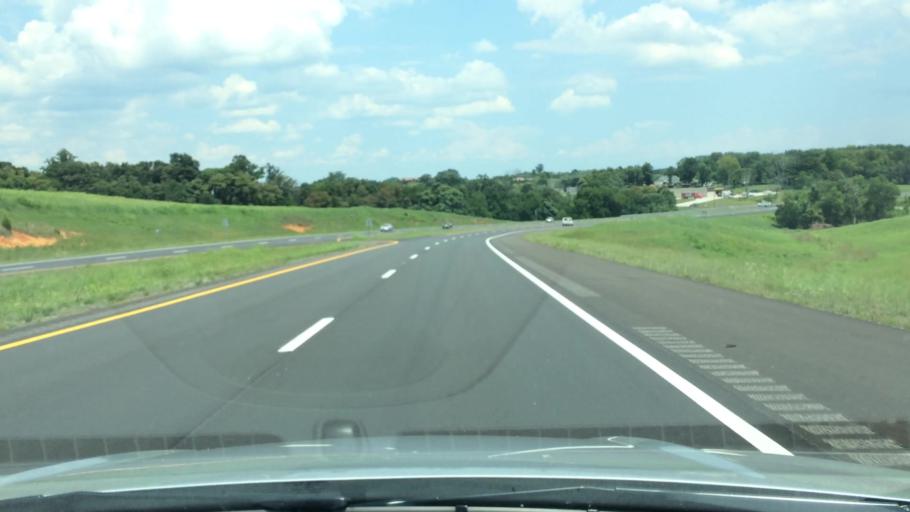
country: US
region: Tennessee
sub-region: Hamblen County
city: Morristown
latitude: 36.1826
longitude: -83.2401
